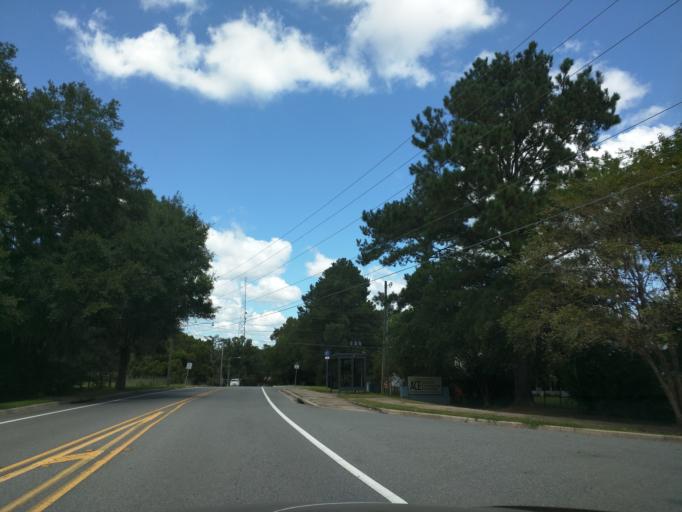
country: US
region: Florida
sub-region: Leon County
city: Tallahassee
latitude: 30.4378
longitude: -84.2188
